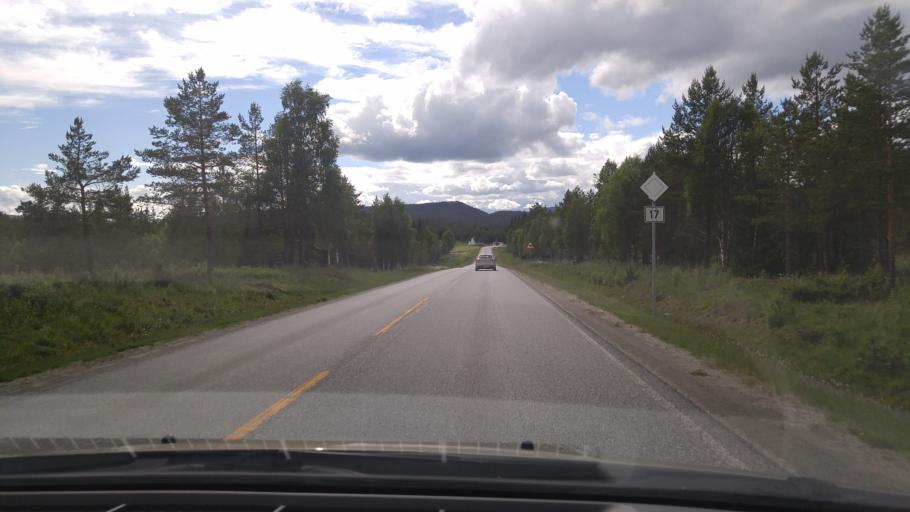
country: NO
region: Nord-Trondelag
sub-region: Namsos
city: Namsos
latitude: 64.4019
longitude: 11.4266
